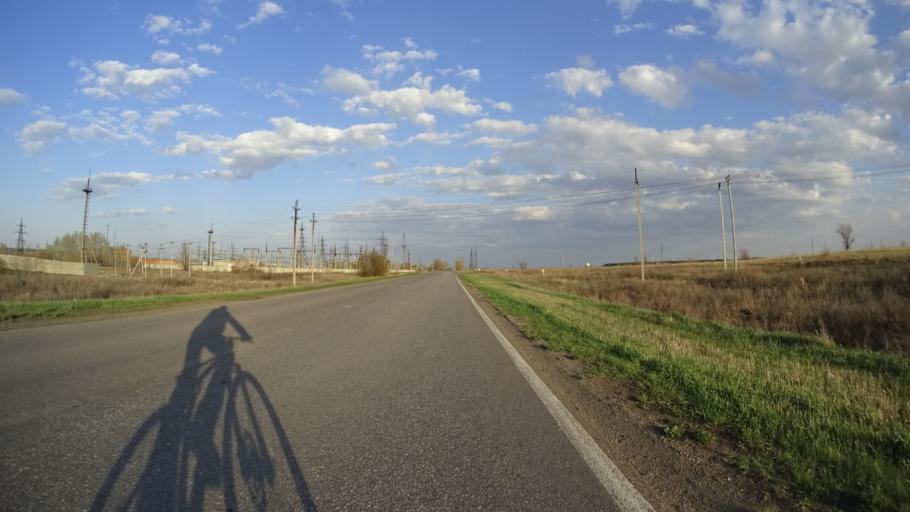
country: RU
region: Chelyabinsk
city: Troitsk
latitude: 54.0594
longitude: 61.5799
